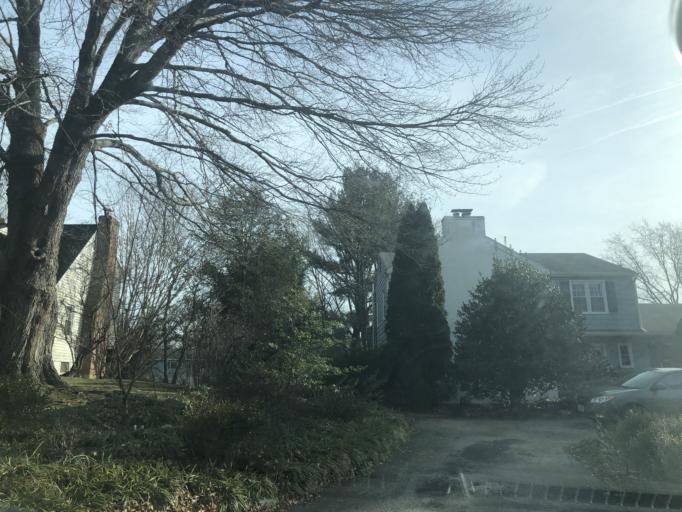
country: US
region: Maryland
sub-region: Howard County
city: Columbia
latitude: 39.2851
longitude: -76.8394
